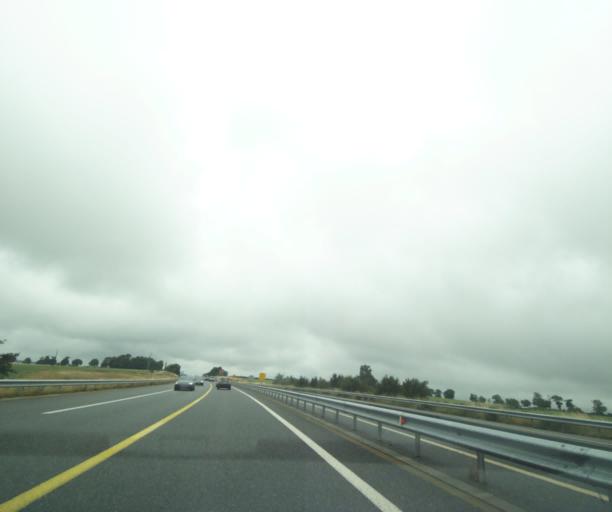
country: FR
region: Midi-Pyrenees
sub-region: Departement de l'Aveyron
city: Luc-la-Primaube
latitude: 44.2940
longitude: 2.5204
